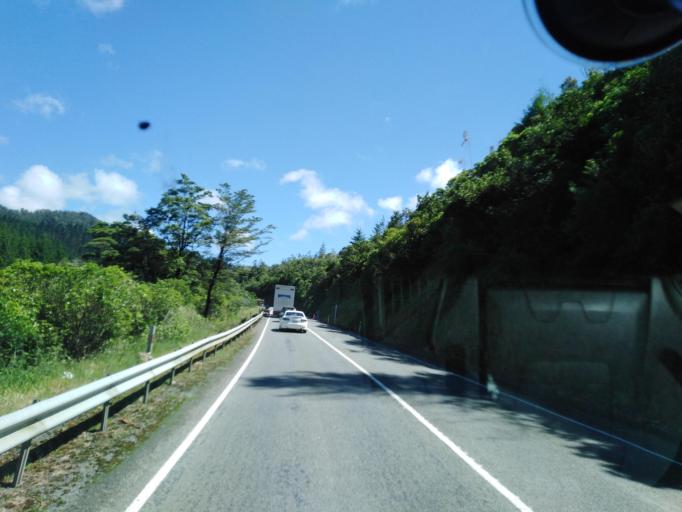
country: NZ
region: Nelson
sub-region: Nelson City
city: Nelson
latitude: -41.1993
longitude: 173.5612
